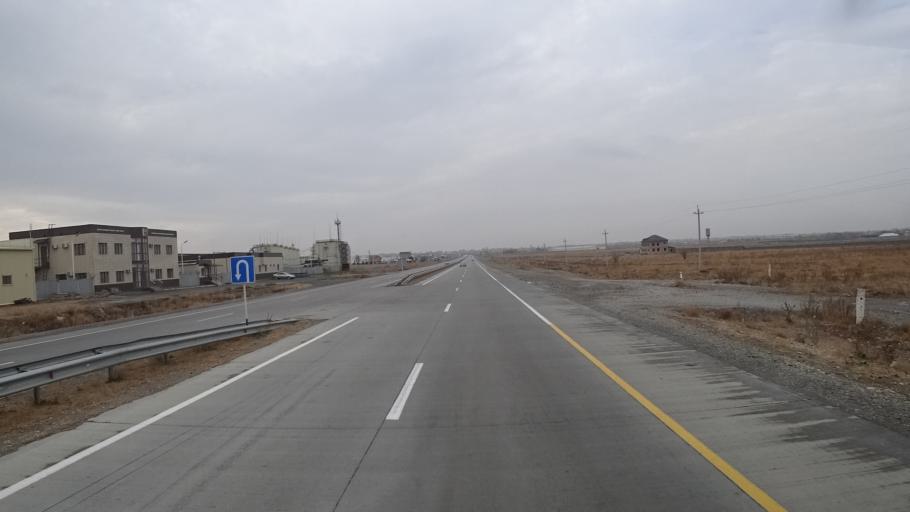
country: KZ
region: Ongtustik Qazaqstan
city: Aksu
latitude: 42.4774
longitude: 69.8365
